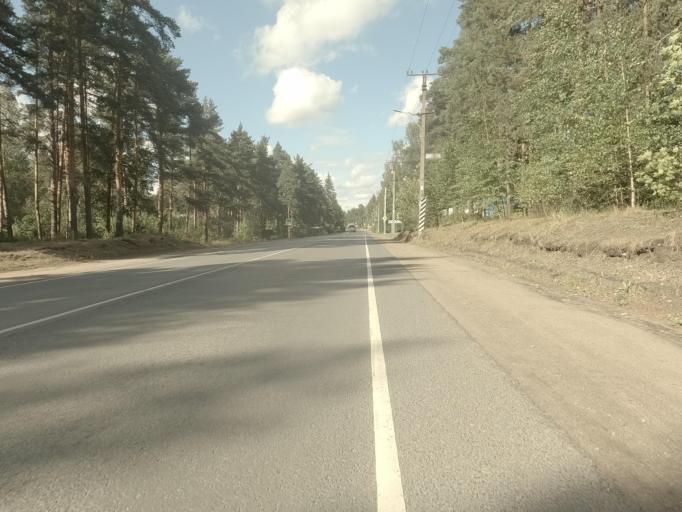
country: RU
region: Leningrad
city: Vsevolozhsk
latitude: 60.0085
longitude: 30.6653
